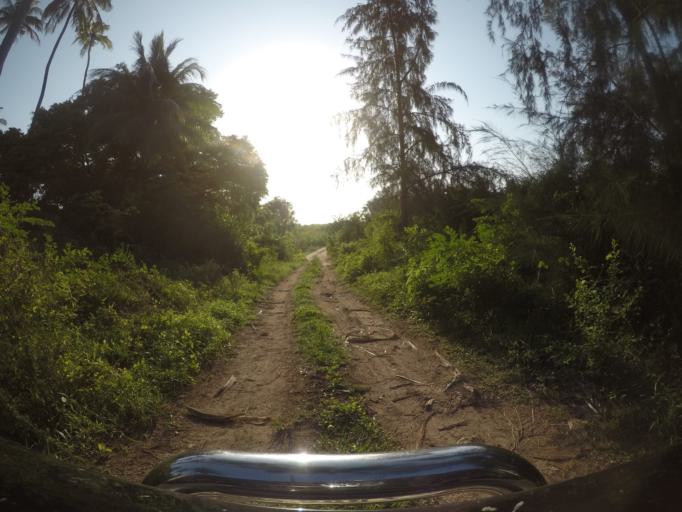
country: TZ
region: Zanzibar Central/South
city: Nganane
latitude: -6.2093
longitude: 39.5329
